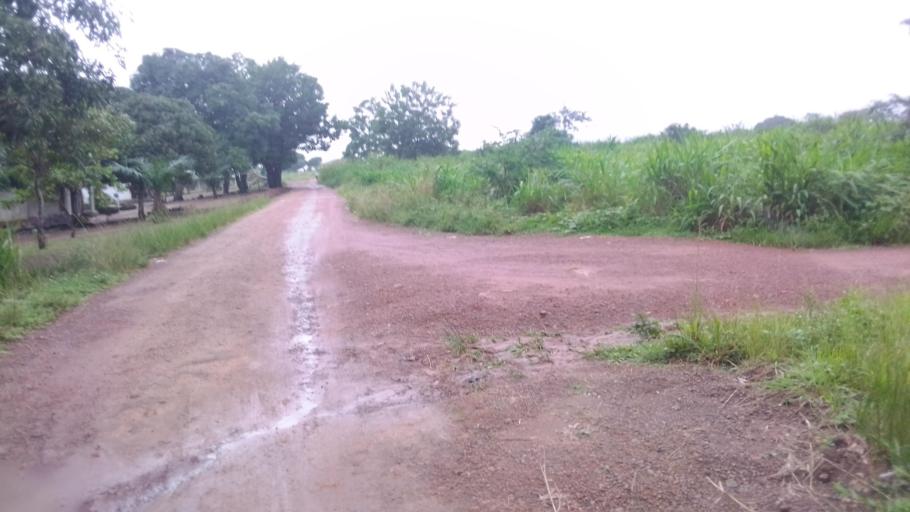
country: SL
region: Eastern Province
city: Kenema
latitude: 7.8984
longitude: -11.1712
